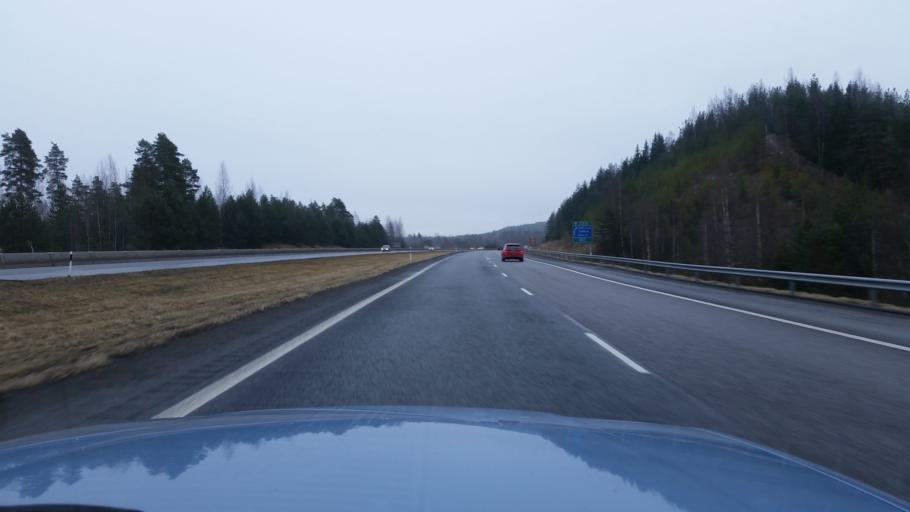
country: FI
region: Haeme
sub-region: Haemeenlinna
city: Parola
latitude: 61.0578
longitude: 24.3424
